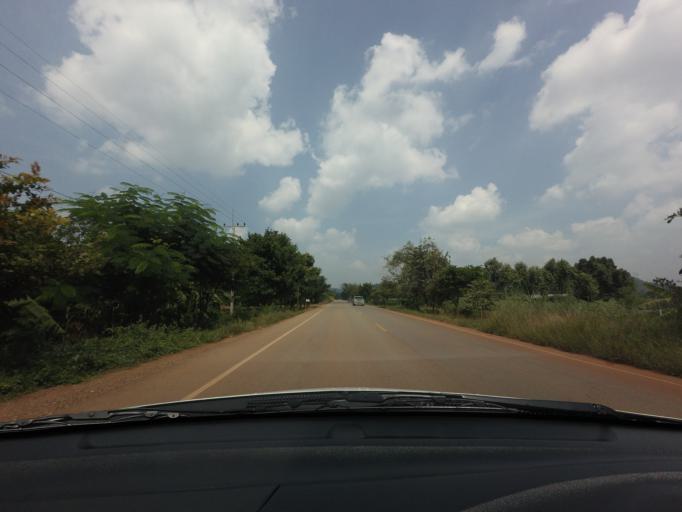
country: TH
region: Nakhon Ratchasima
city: Pak Chong
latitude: 14.5683
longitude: 101.5701
